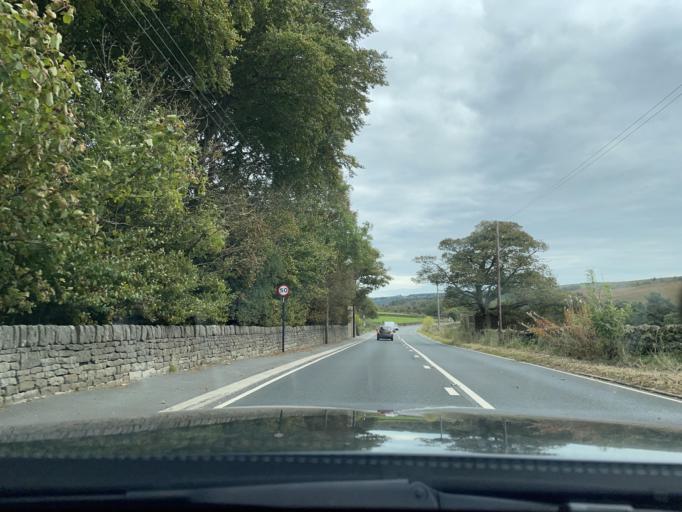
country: GB
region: England
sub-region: Sheffield
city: Bradfield
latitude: 53.3866
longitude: -1.6137
